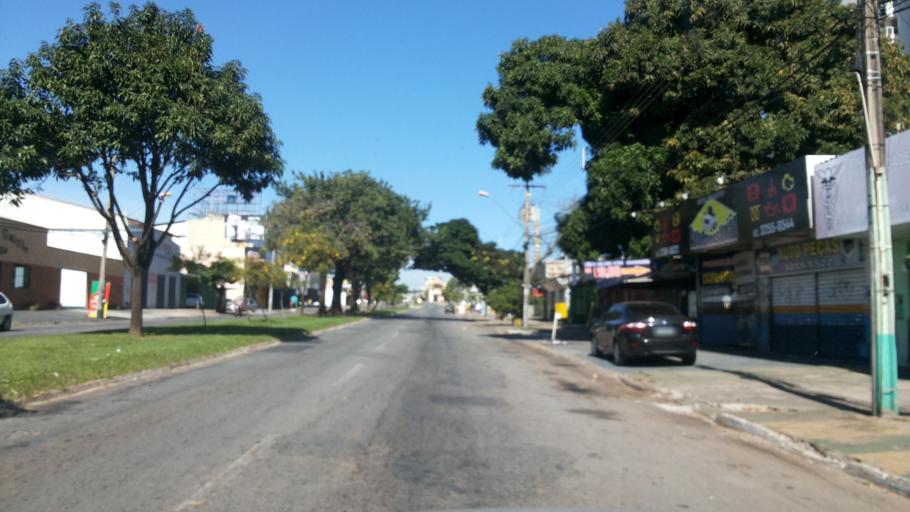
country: BR
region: Goias
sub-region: Goiania
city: Goiania
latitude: -16.7181
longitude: -49.2570
